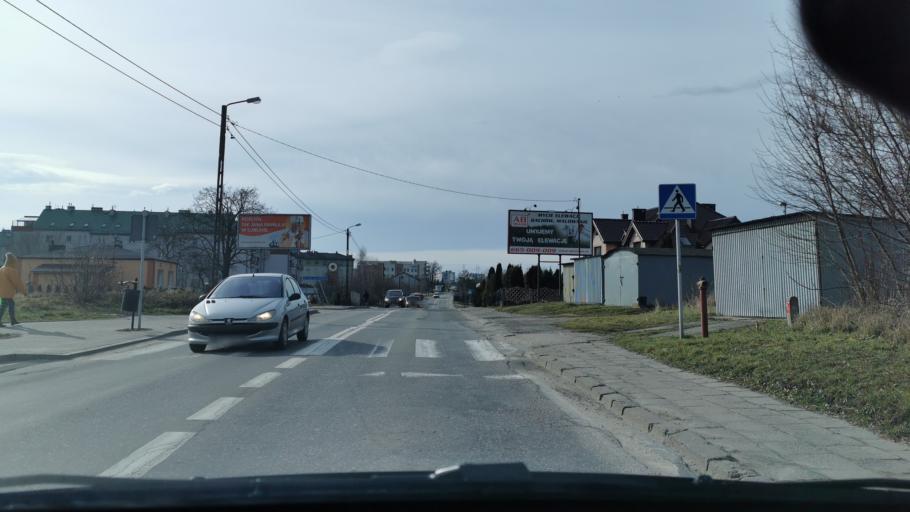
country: PL
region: Lublin Voivodeship
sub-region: Powiat lubelski
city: Lublin
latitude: 51.2027
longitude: 22.5432
